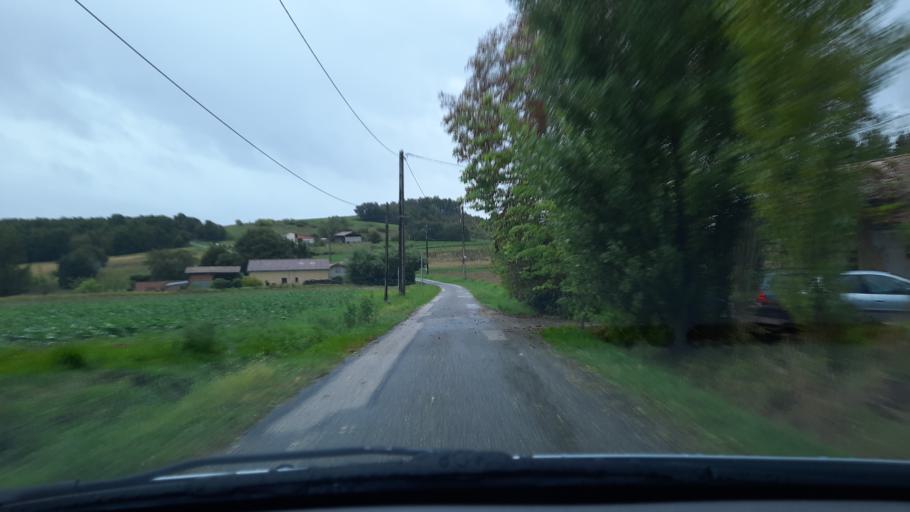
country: FR
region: Midi-Pyrenees
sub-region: Departement du Tarn-et-Garonne
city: Molieres
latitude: 44.1897
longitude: 1.3071
